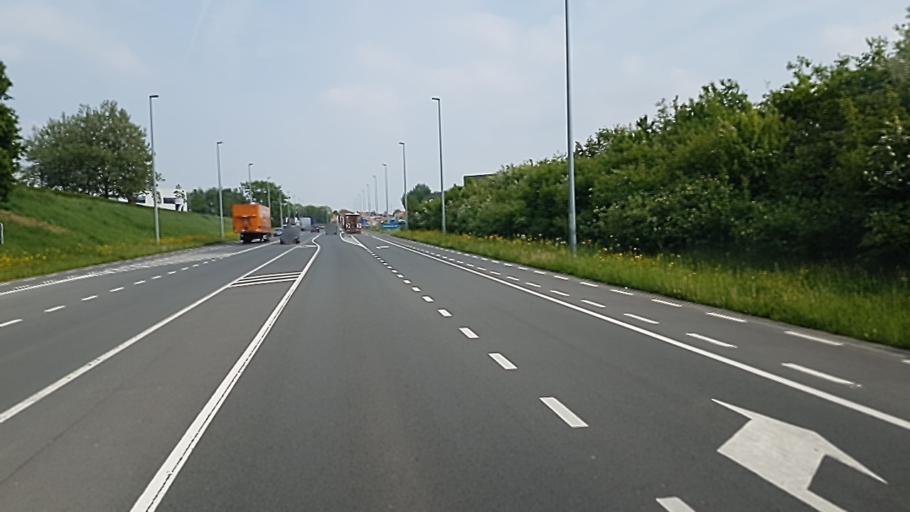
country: BE
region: Flanders
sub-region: Provincie West-Vlaanderen
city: Kortrijk
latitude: 50.8024
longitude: 3.2787
